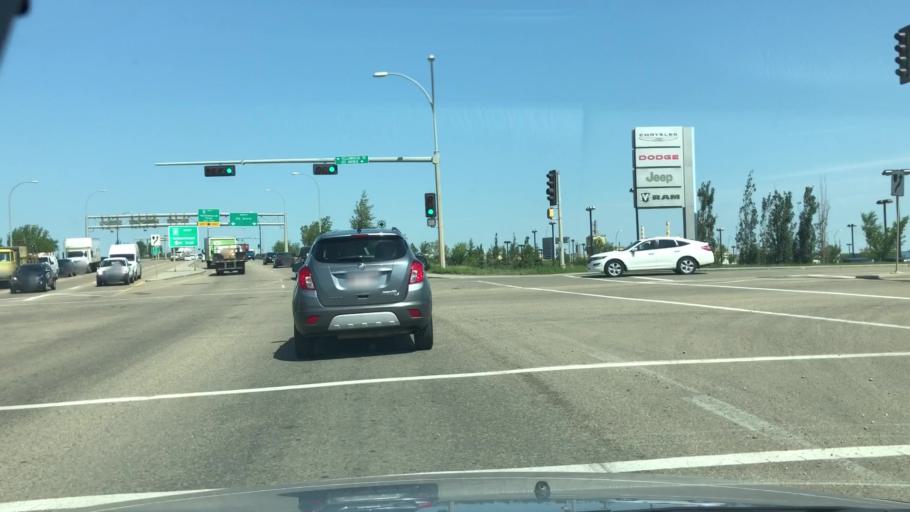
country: CA
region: Alberta
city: St. Albert
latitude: 53.5773
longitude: -113.5902
